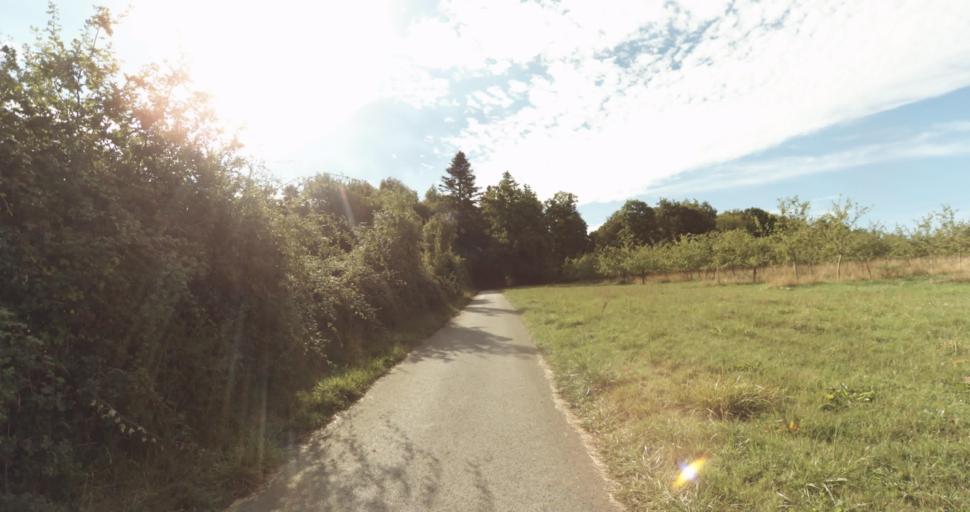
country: FR
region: Lower Normandy
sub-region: Departement de l'Orne
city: Gace
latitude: 48.8297
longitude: 0.2292
